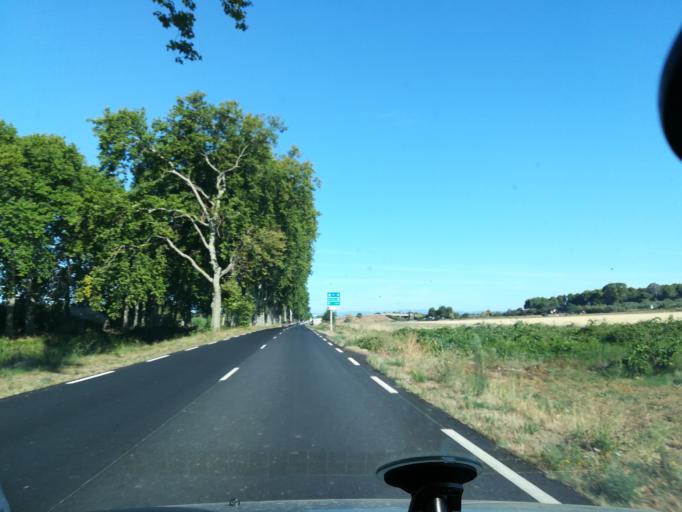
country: FR
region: Languedoc-Roussillon
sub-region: Departement de l'Herault
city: Portiragnes
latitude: 43.3109
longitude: 3.3199
